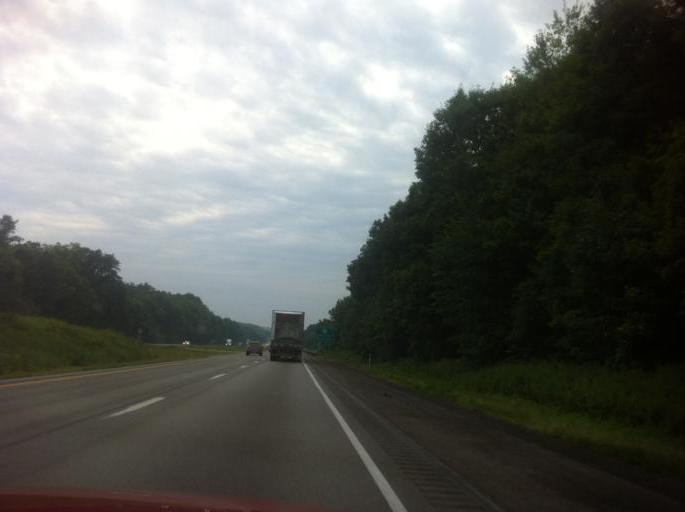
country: US
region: Pennsylvania
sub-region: Mercer County
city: Grove City
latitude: 41.2011
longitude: -80.0497
